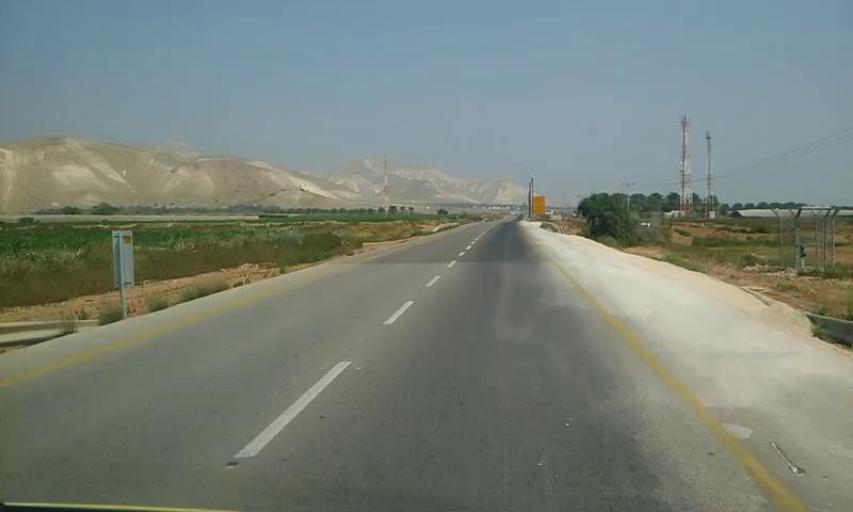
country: PS
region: West Bank
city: Al Fasayil
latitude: 32.0399
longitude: 35.4585
